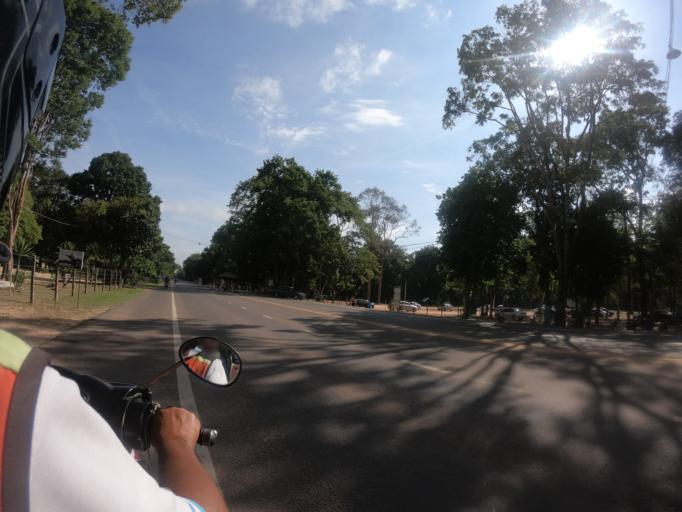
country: TH
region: Surin
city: Kap Choeng
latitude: 14.4405
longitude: 103.7007
